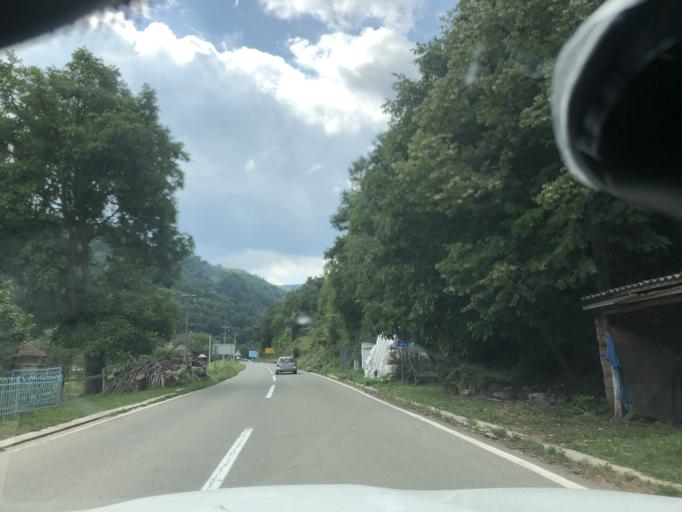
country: RS
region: Central Serbia
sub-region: Jablanicki Okrug
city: Medvega
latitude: 42.8047
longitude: 21.5779
